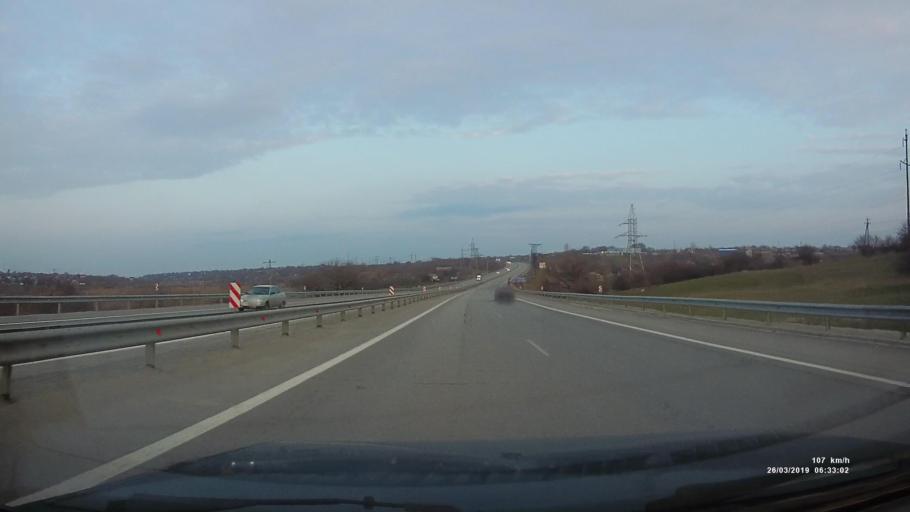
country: RU
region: Rostov
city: Chaltyr
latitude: 47.2712
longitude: 39.4983
